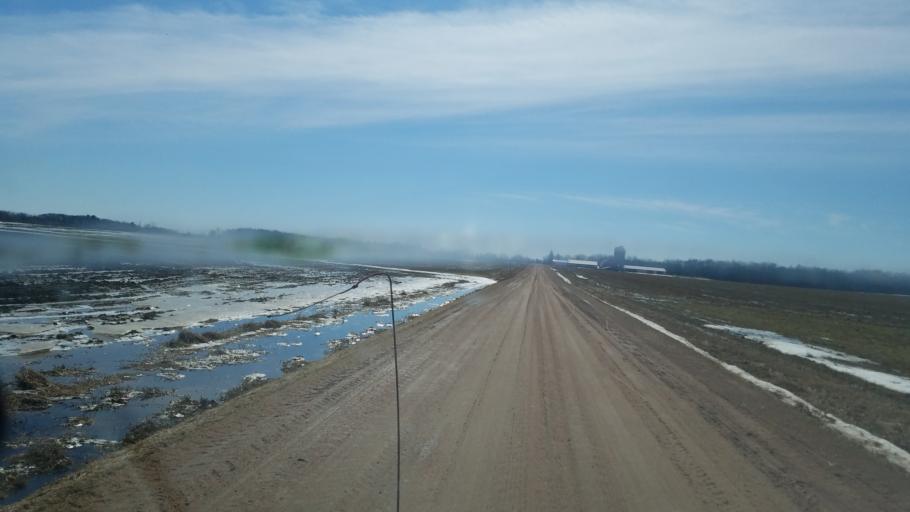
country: US
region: Wisconsin
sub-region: Clark County
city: Loyal
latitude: 44.6394
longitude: -90.4076
